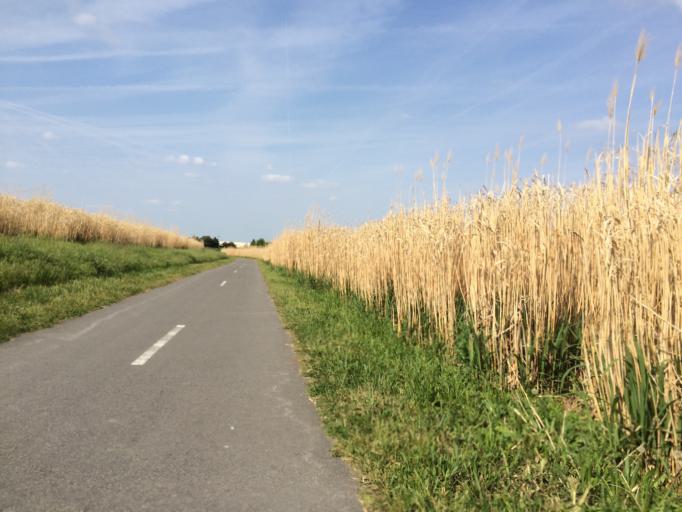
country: FR
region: Ile-de-France
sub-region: Departement de l'Essonne
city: Chilly-Mazarin
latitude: 48.7106
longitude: 2.3143
